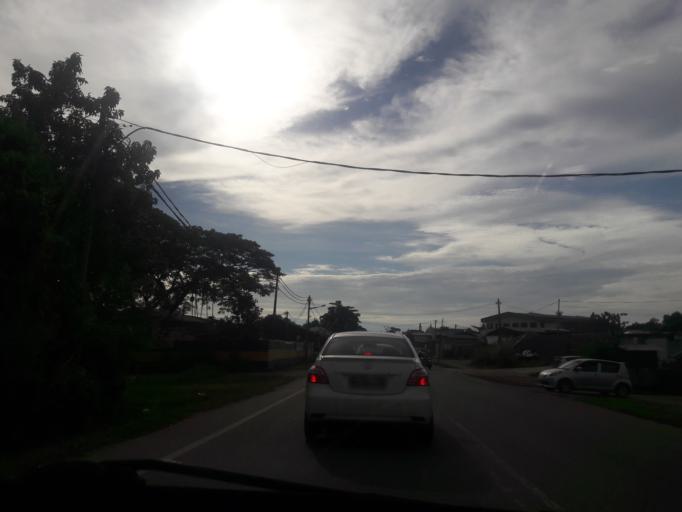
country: MY
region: Kedah
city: Sungai Petani
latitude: 5.6342
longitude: 100.5046
